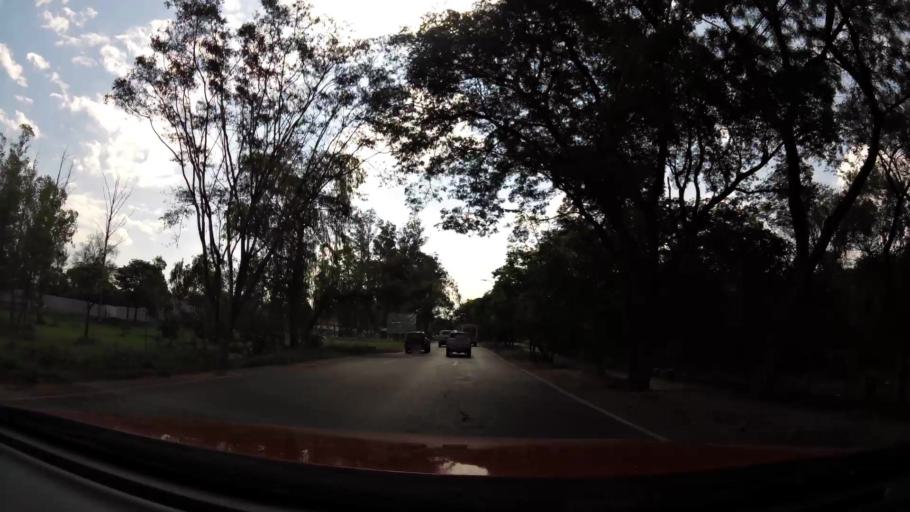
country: PY
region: Central
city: Fernando de la Mora
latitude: -25.3407
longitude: -57.5185
